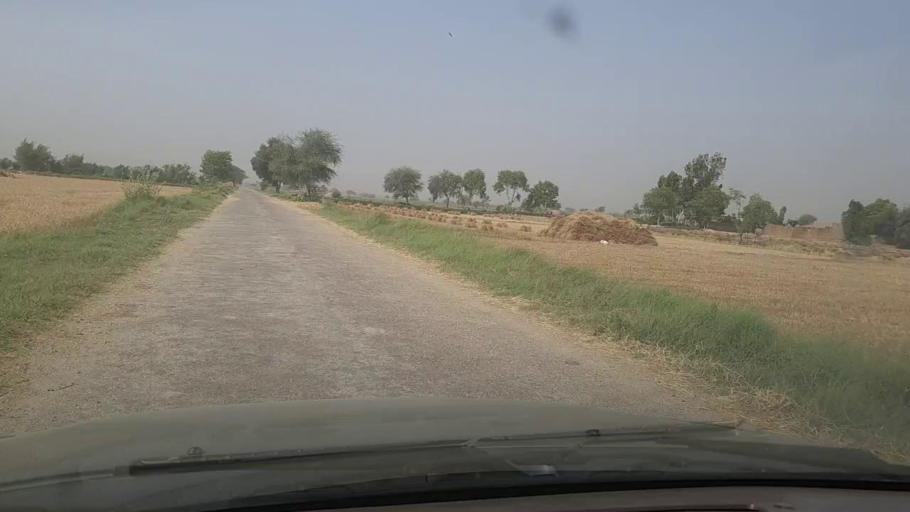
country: PK
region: Sindh
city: Garhi Yasin
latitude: 27.8861
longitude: 68.5748
